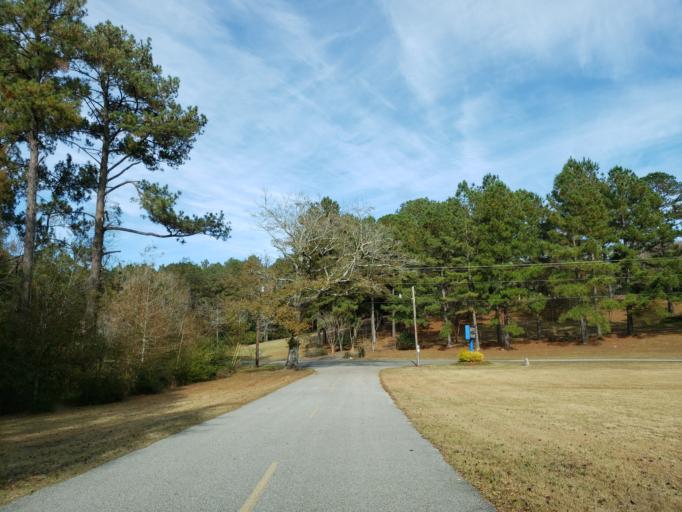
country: US
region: Mississippi
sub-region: Forrest County
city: Rawls Springs
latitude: 31.3963
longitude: -89.3605
